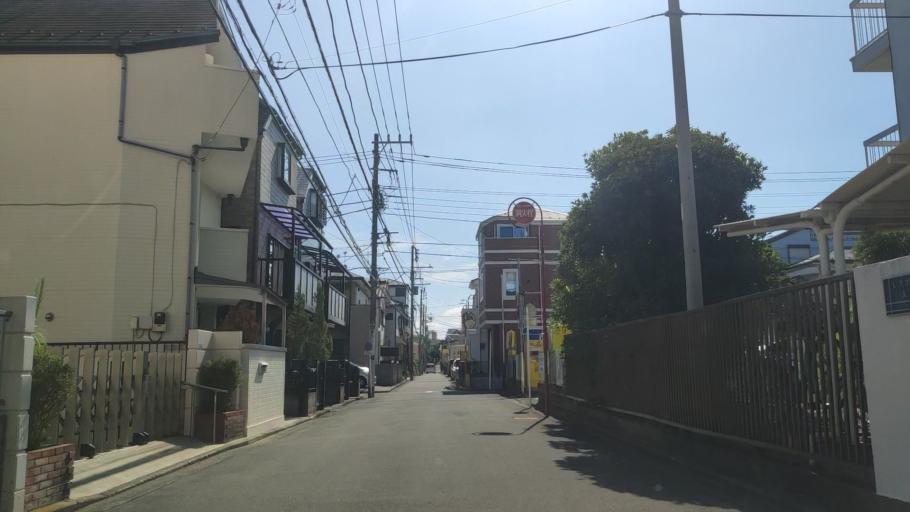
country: JP
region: Kanagawa
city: Yokohama
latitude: 35.5198
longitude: 139.6227
